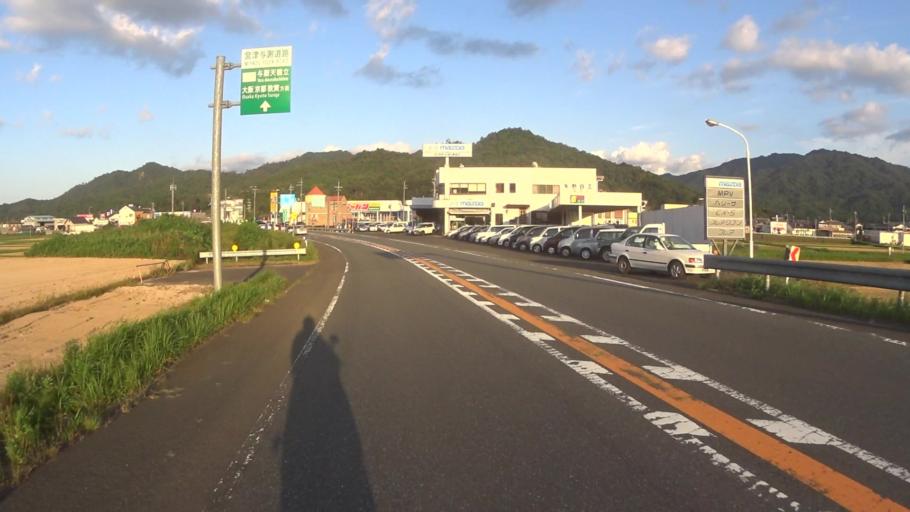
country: JP
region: Kyoto
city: Miyazu
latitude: 35.5346
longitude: 135.1203
